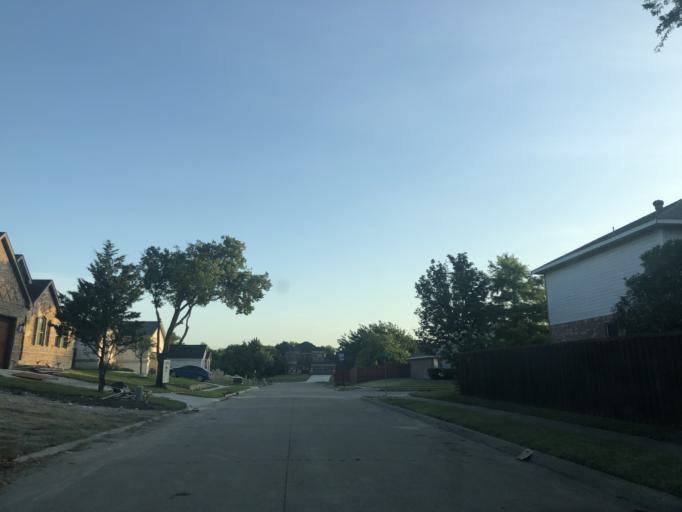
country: US
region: Texas
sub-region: Dallas County
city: Duncanville
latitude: 32.6464
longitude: -96.9565
